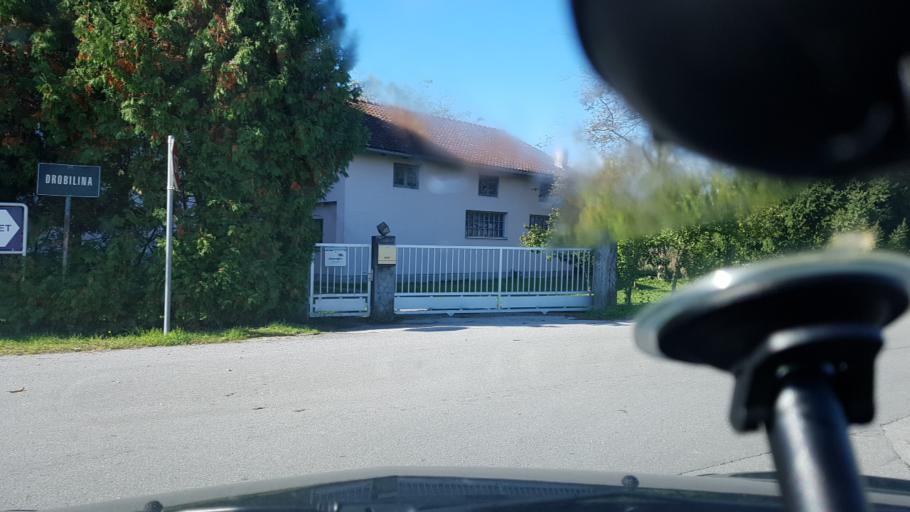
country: HR
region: Grad Zagreb
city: Lucko
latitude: 45.7420
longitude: 15.8635
